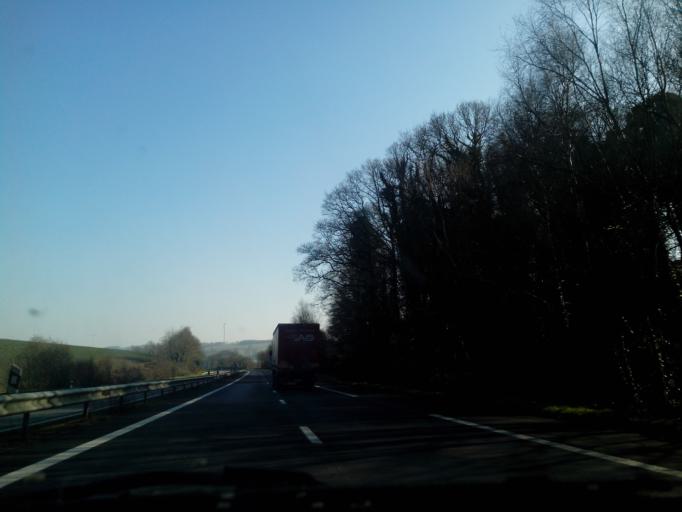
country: FR
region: Brittany
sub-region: Departement des Cotes-d'Armor
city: Plemet
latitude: 48.1715
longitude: -2.6515
